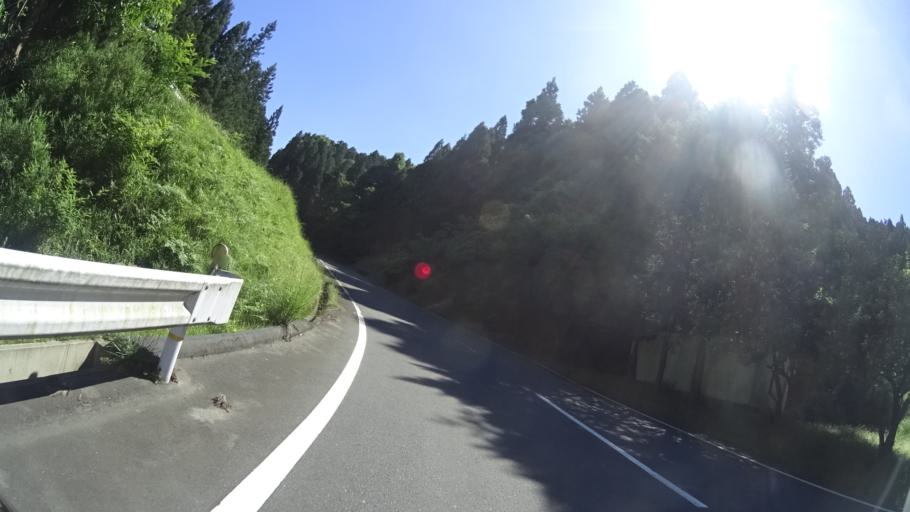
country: JP
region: Kyoto
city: Fukuchiyama
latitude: 35.3971
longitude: 135.0753
